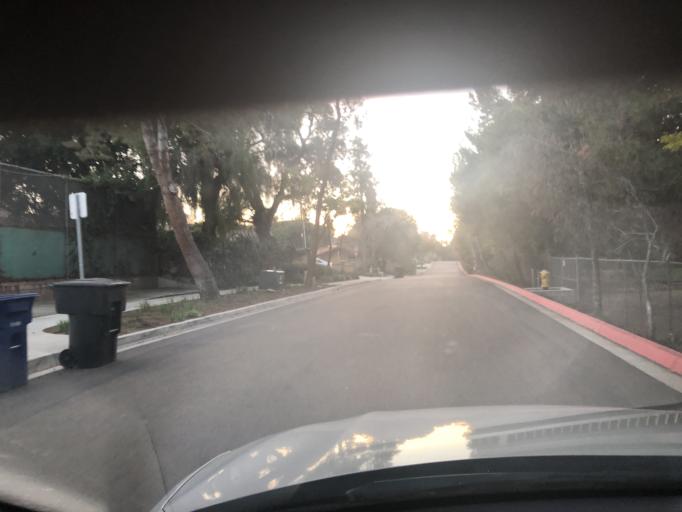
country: US
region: California
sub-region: San Diego County
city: Chula Vista
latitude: 32.6437
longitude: -117.0649
